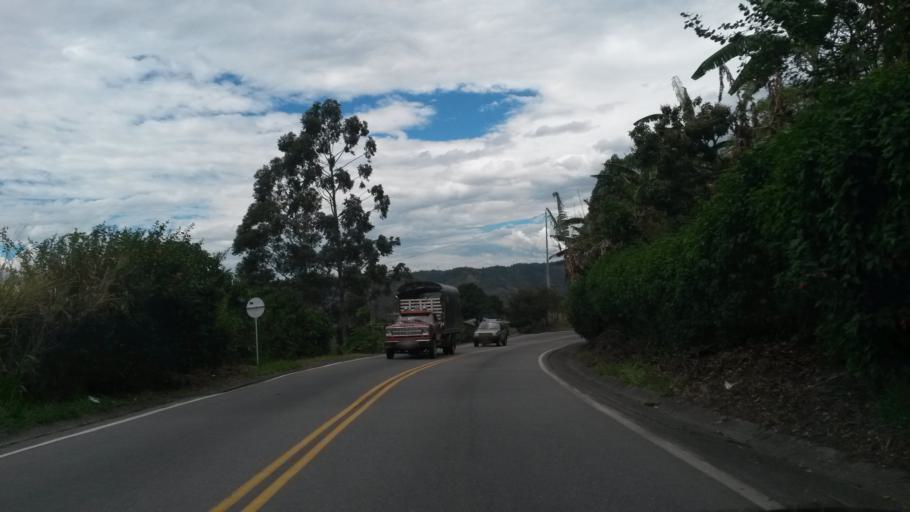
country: CO
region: Cauca
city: Rosas
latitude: 2.2713
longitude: -76.7287
